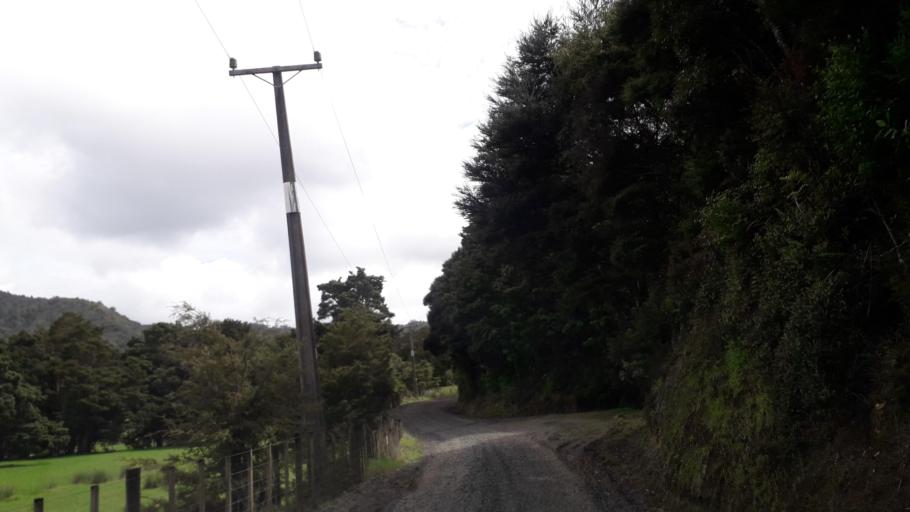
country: NZ
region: Northland
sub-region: Far North District
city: Kaitaia
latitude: -35.2330
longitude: 173.2648
